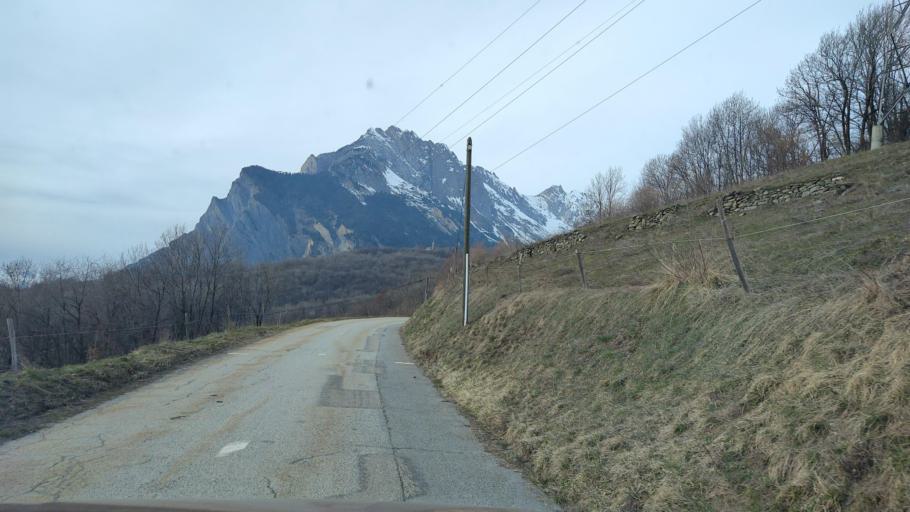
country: FR
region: Rhone-Alpes
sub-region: Departement de la Savoie
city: Saint-Michel-de-Maurienne
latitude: 45.2302
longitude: 6.4703
